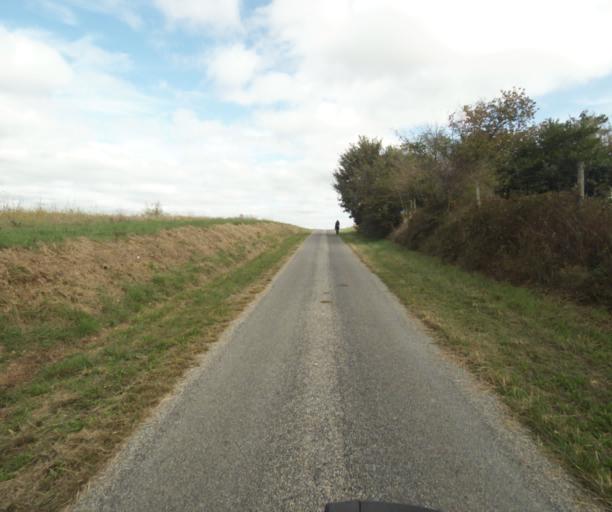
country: FR
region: Midi-Pyrenees
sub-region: Departement du Tarn-et-Garonne
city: Finhan
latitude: 43.9292
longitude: 1.2152
